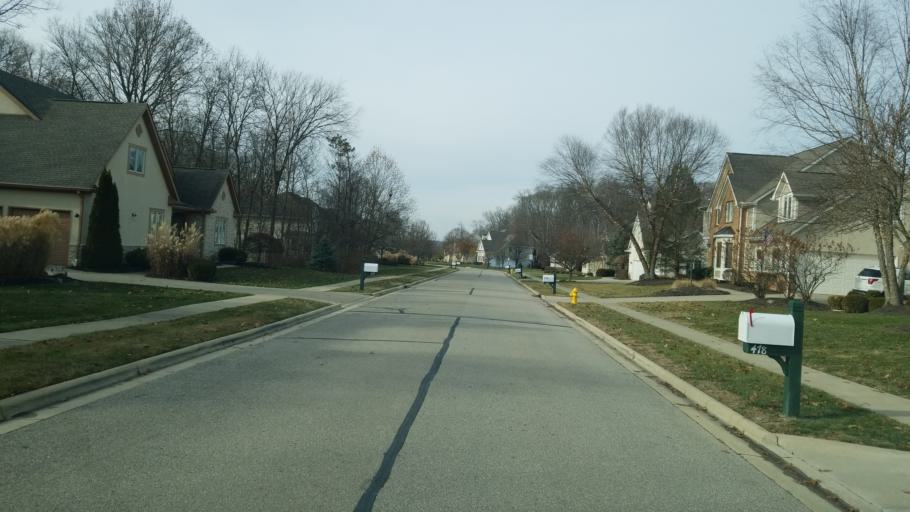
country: US
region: Ohio
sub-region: Delaware County
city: Lewis Center
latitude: 40.1679
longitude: -83.0302
